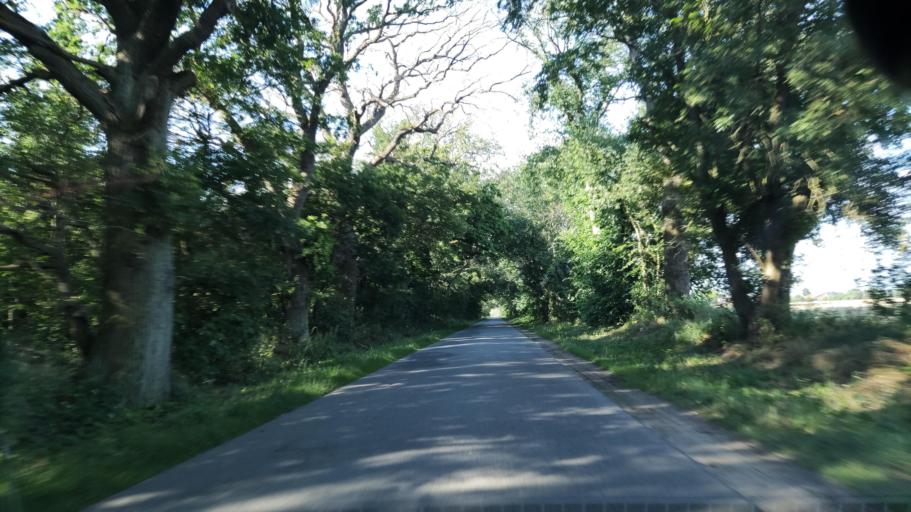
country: DE
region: Lower Saxony
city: Gartow
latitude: 53.0324
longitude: 11.4915
